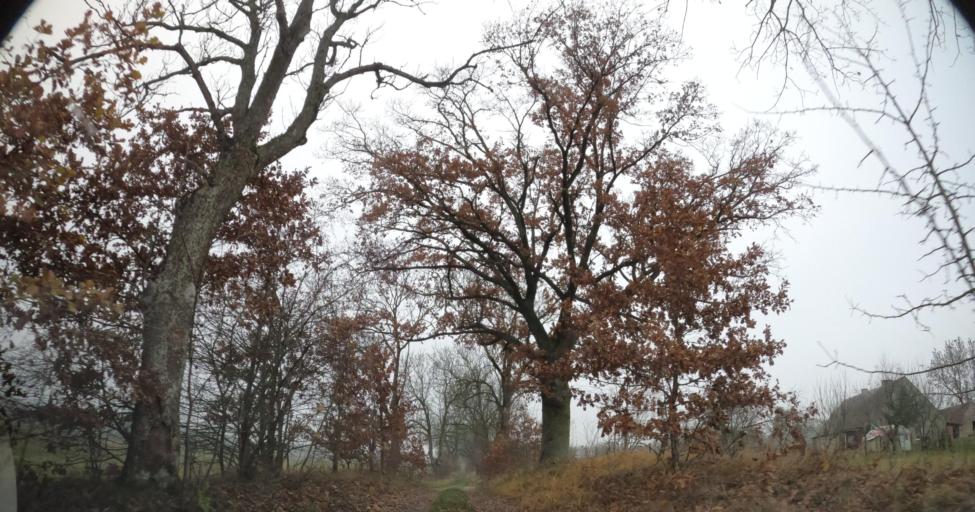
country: PL
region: West Pomeranian Voivodeship
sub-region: Powiat drawski
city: Drawsko Pomorskie
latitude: 53.5932
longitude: 15.7893
